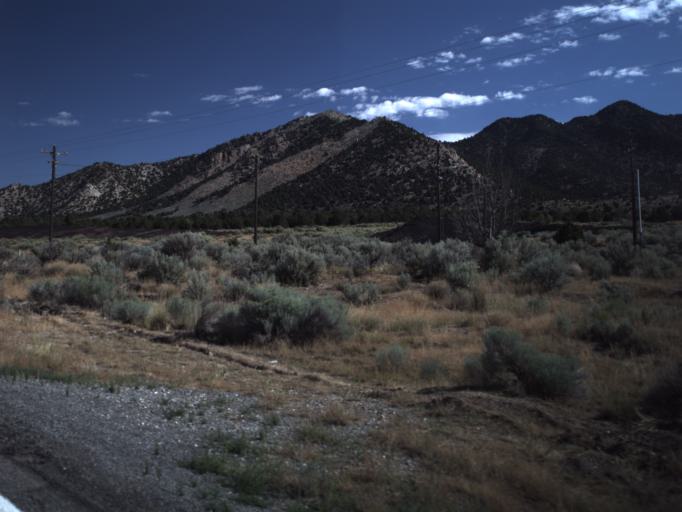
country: US
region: Utah
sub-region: Juab County
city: Mona
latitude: 39.9159
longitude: -112.1431
